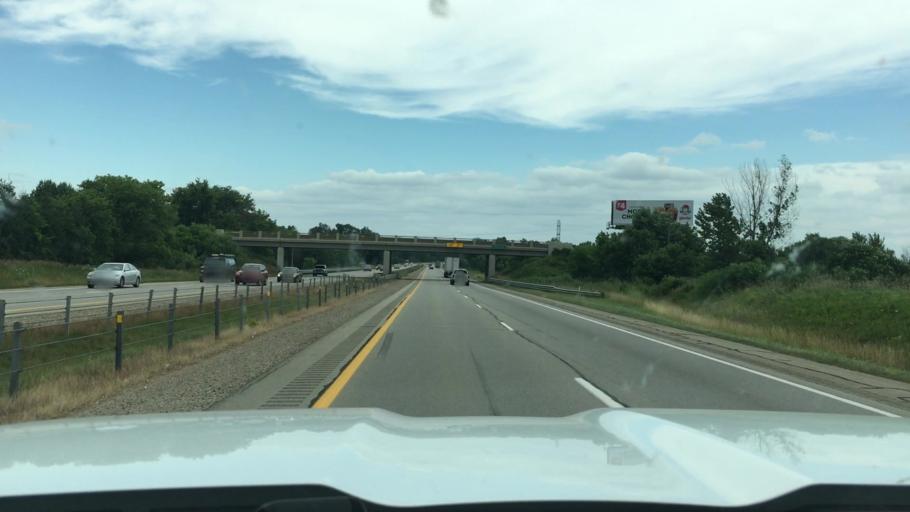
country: US
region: Michigan
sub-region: Kent County
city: Byron Center
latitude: 42.7527
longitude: -85.6734
